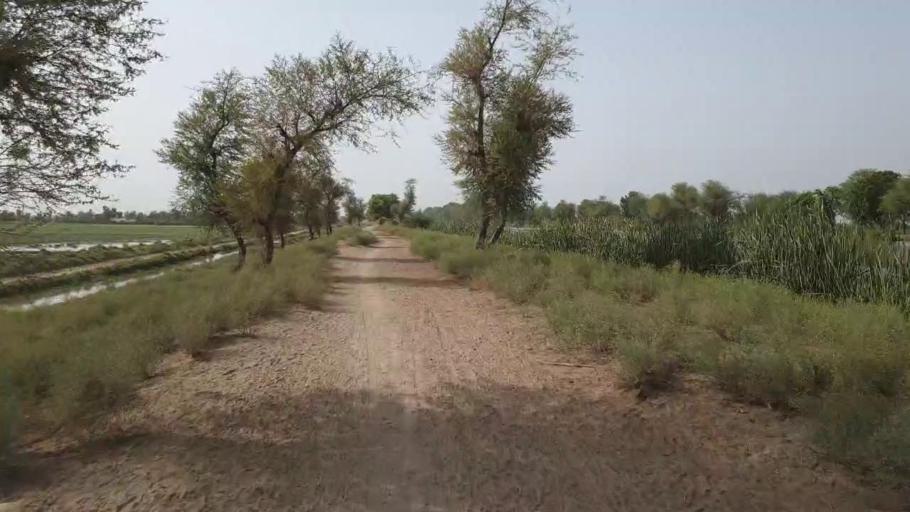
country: PK
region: Sindh
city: Daur
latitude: 26.4468
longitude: 68.1602
